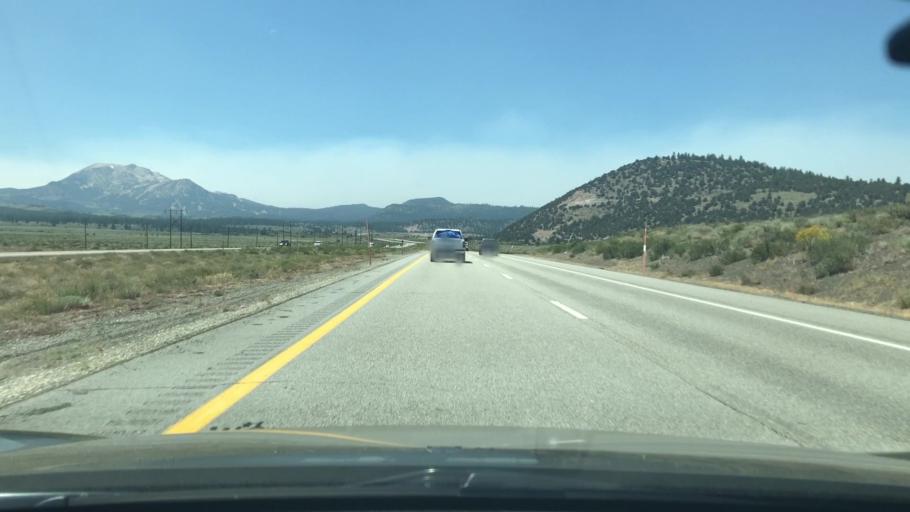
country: US
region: California
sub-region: Mono County
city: Mammoth Lakes
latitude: 37.6333
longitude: -118.8756
